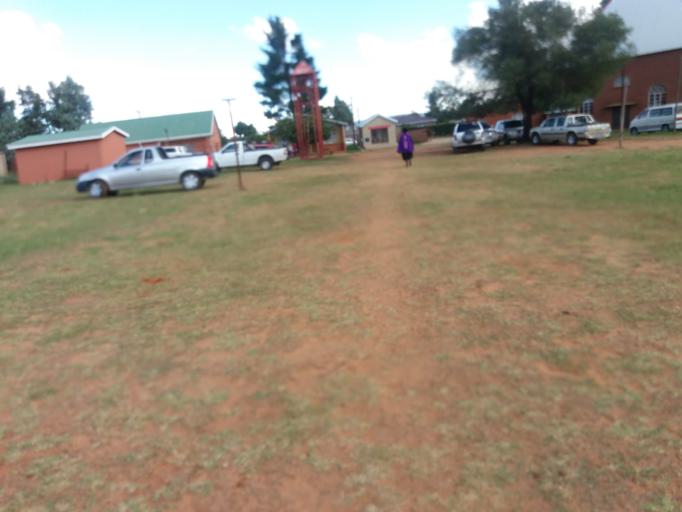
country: LS
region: Maseru
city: Maseru
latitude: -29.3714
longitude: 27.5066
